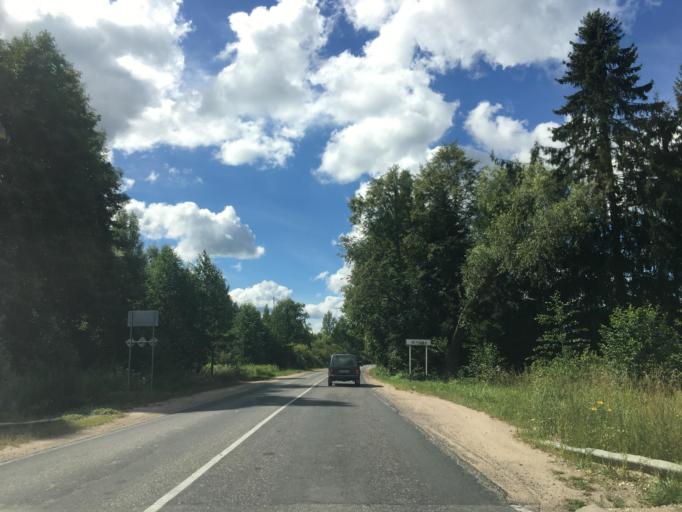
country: RU
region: Pskov
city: Pskov
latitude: 57.6950
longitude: 28.1796
